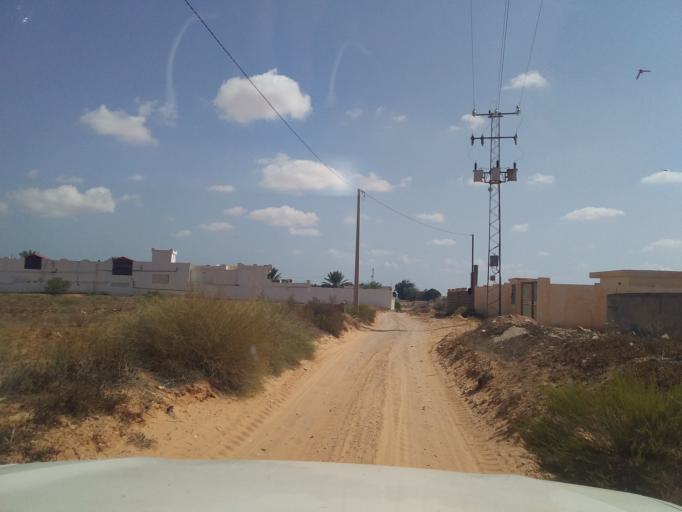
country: TN
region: Madanin
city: Medenine
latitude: 33.6008
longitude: 10.3156
